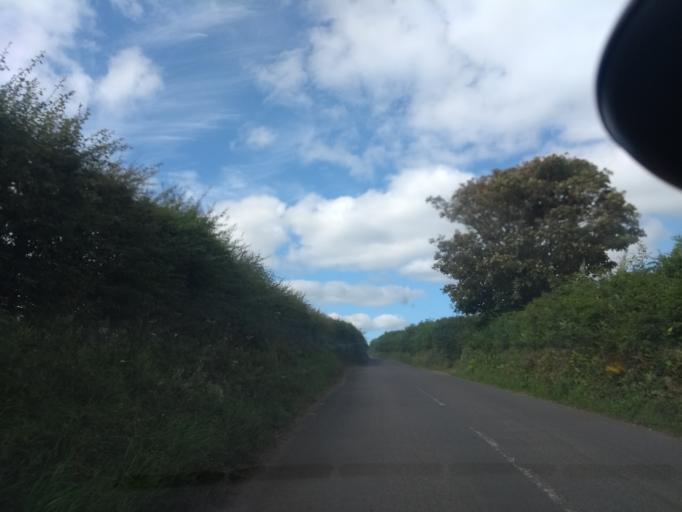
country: GB
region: England
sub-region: Devon
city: Modbury
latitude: 50.2994
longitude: -3.8898
